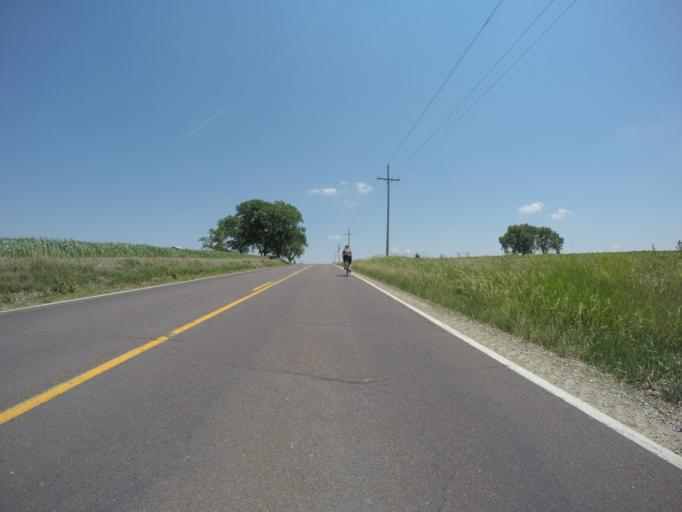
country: US
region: Kansas
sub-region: Doniphan County
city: Troy
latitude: 39.7400
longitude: -95.1539
